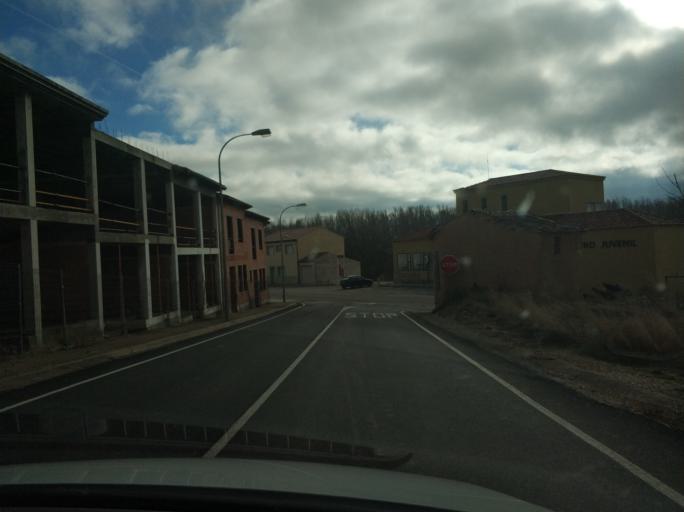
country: ES
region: Castille and Leon
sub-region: Provincia de Soria
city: San Esteban de Gormaz
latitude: 41.5752
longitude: -3.2097
